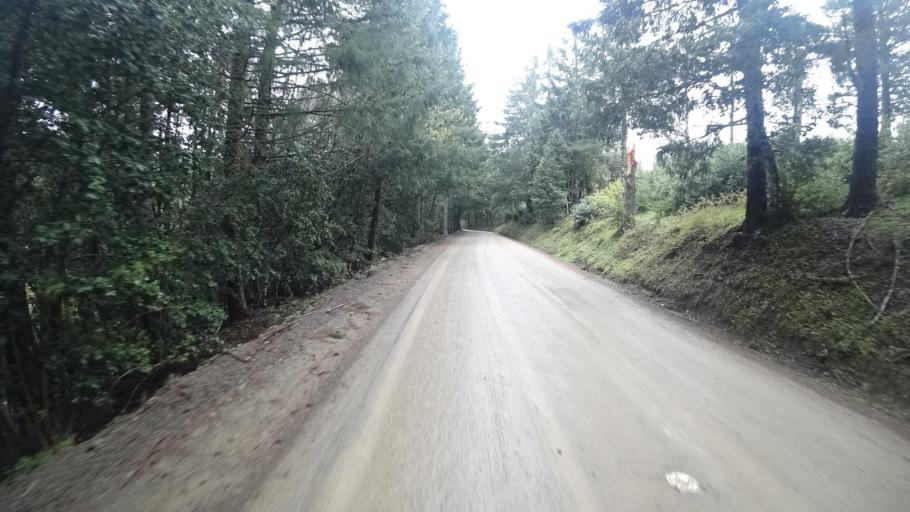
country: US
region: California
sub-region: Humboldt County
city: Westhaven-Moonstone
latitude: 41.1407
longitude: -123.8608
